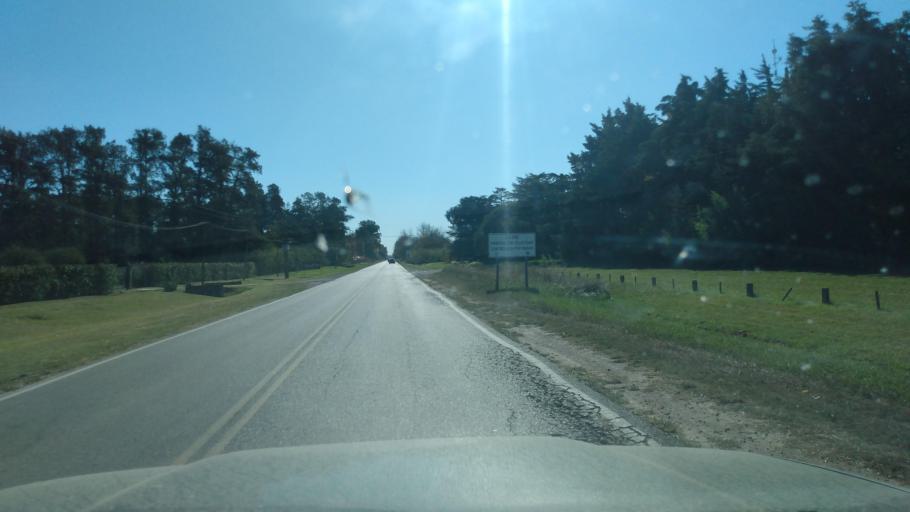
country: AR
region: Buenos Aires
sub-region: Partido de Lujan
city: Lujan
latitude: -34.5420
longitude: -59.1590
